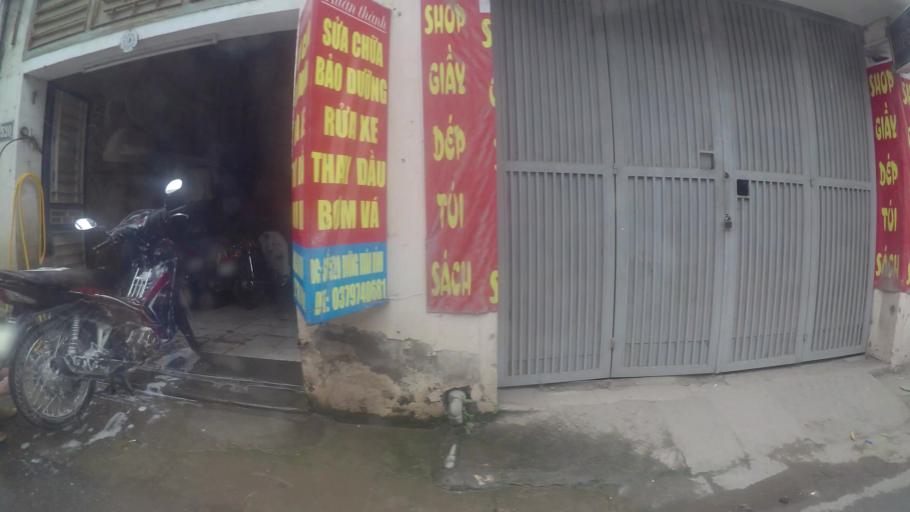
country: VN
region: Ha Noi
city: Tay Ho
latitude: 21.0752
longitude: 105.7882
